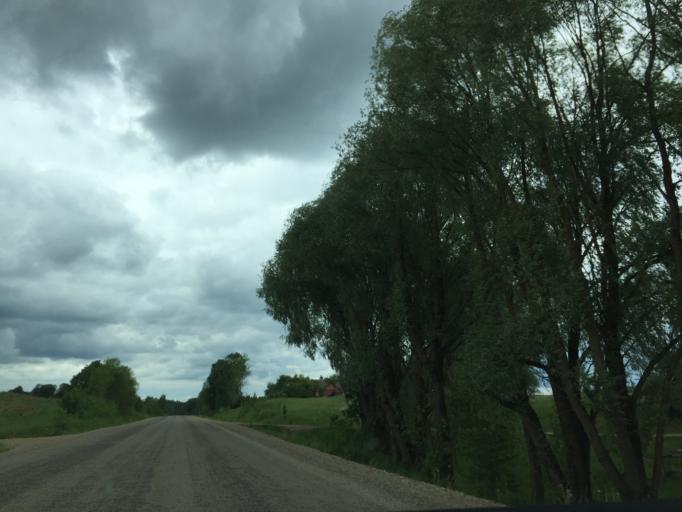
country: LV
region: Dagda
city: Dagda
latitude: 56.0766
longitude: 27.5423
